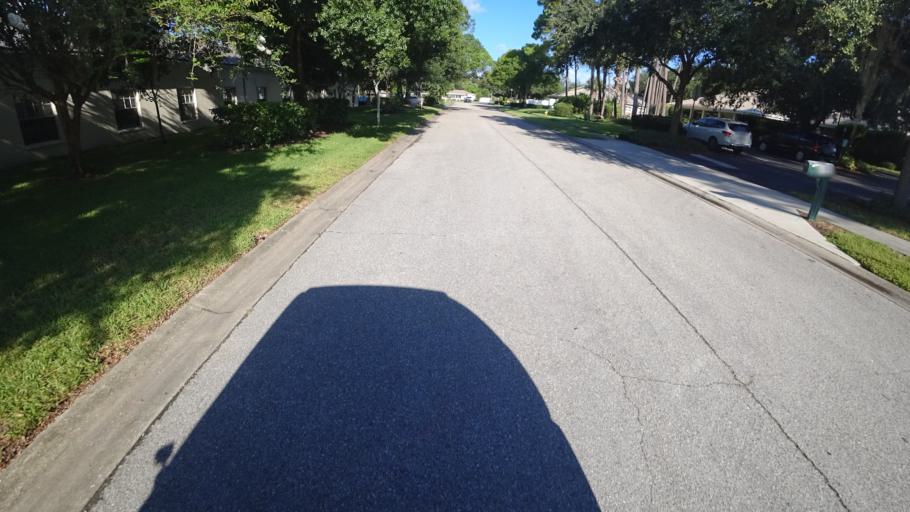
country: US
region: Florida
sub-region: Manatee County
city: South Bradenton
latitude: 27.4703
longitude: -82.5863
